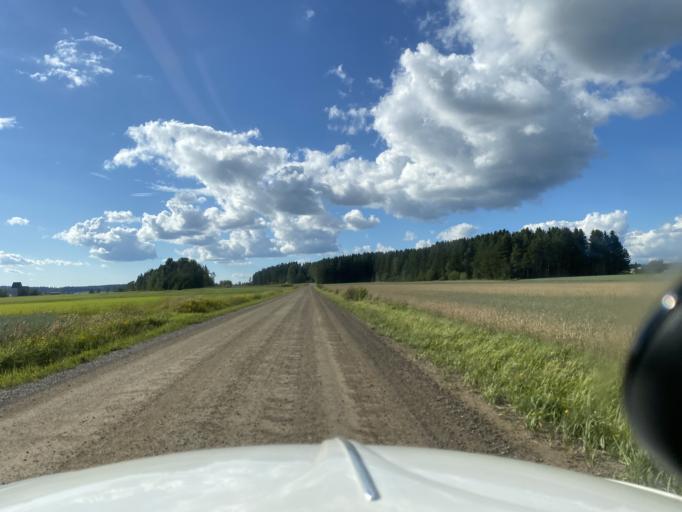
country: FI
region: Pirkanmaa
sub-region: Lounais-Pirkanmaa
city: Punkalaidun
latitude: 61.1358
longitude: 23.2244
